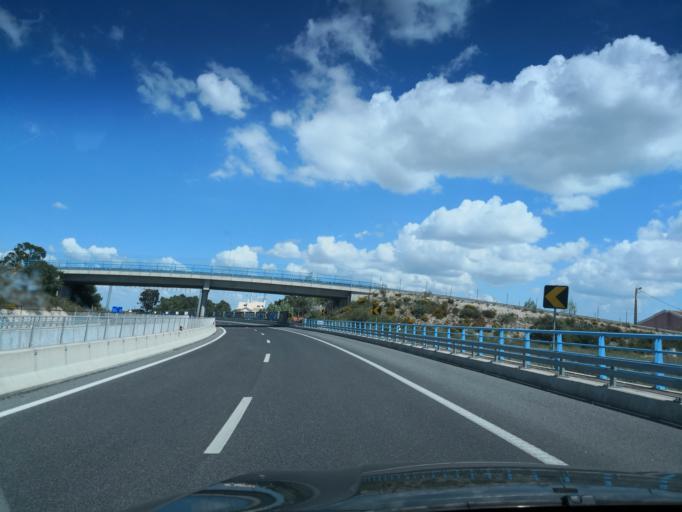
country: PT
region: Setubal
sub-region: Almada
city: Charneca
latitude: 38.6107
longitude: -9.1639
